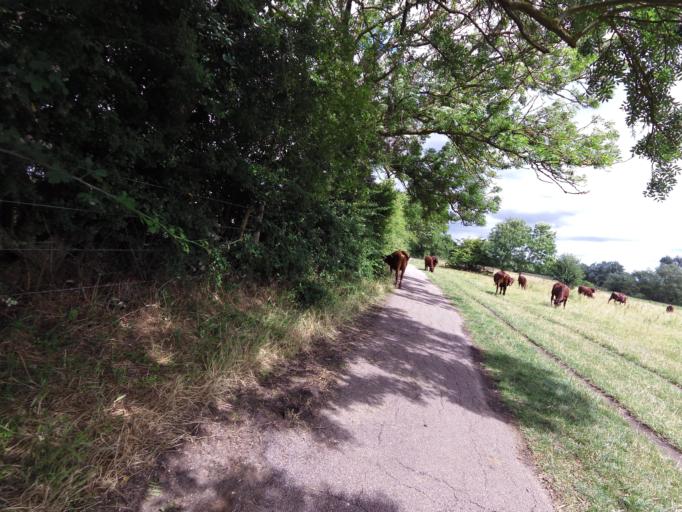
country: GB
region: England
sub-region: Cambridgeshire
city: Grantchester
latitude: 52.1865
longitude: 0.1005
